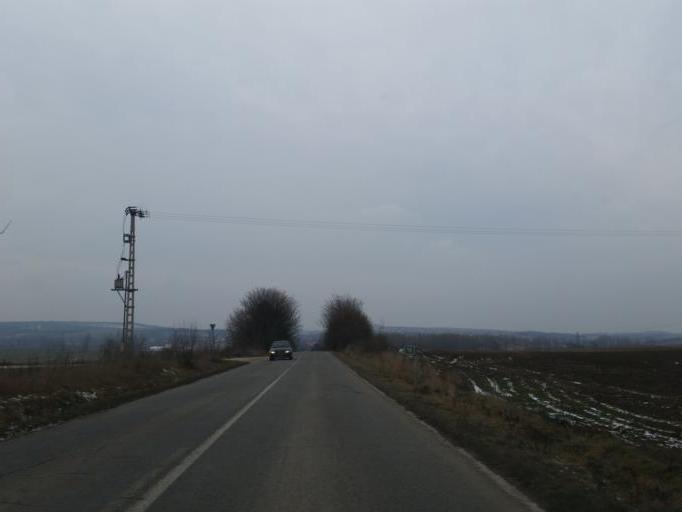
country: HU
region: Pest
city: Perbal
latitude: 47.5749
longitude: 18.7807
